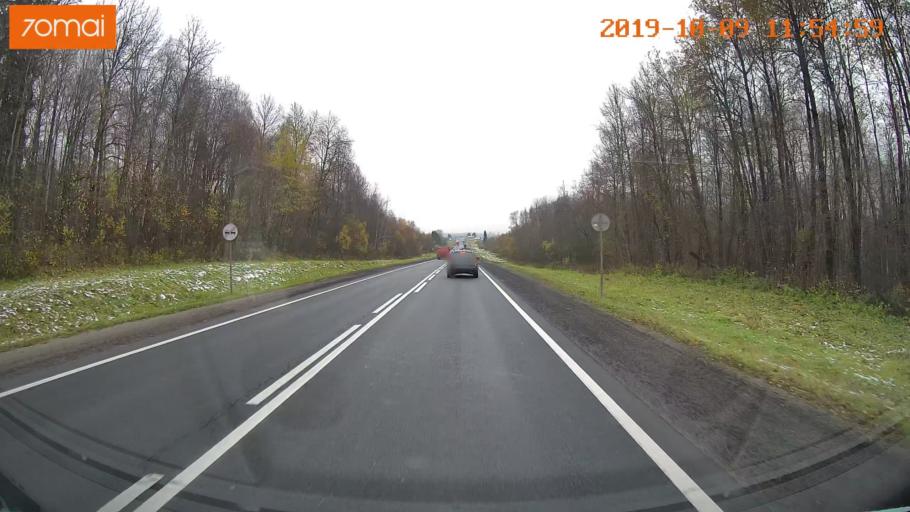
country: RU
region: Vologda
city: Gryazovets
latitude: 58.7527
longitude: 40.2840
